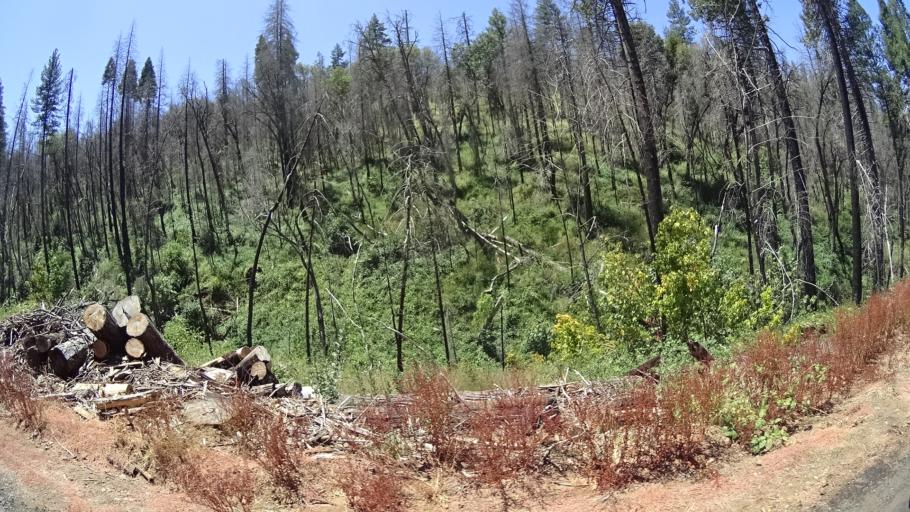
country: US
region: California
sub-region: Calaveras County
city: Mountain Ranch
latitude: 38.2516
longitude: -120.5793
